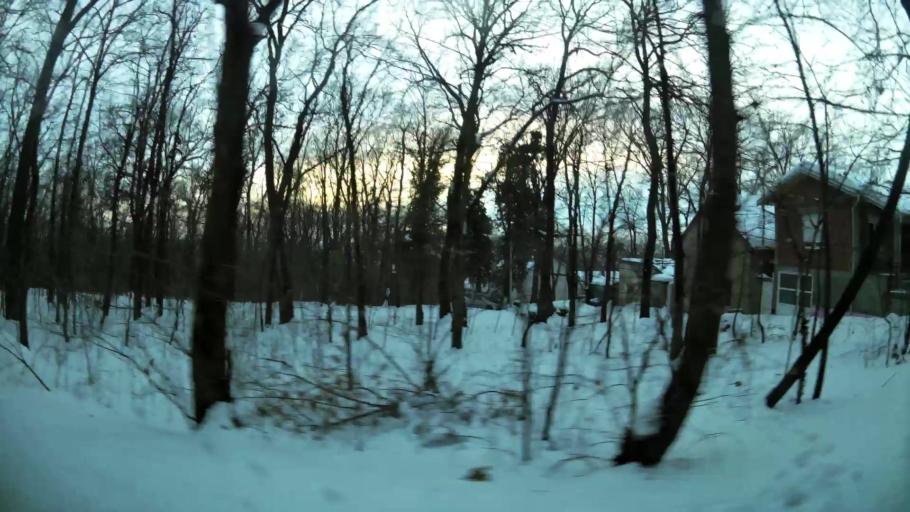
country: RS
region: Central Serbia
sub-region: Belgrade
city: Palilula
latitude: 44.8018
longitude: 20.5054
